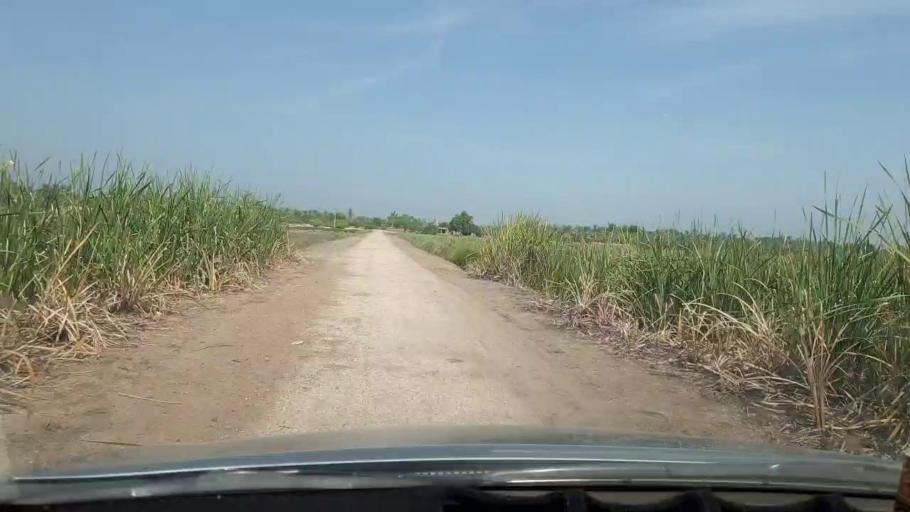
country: PK
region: Sindh
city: Khairpur
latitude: 27.4716
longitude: 68.7443
